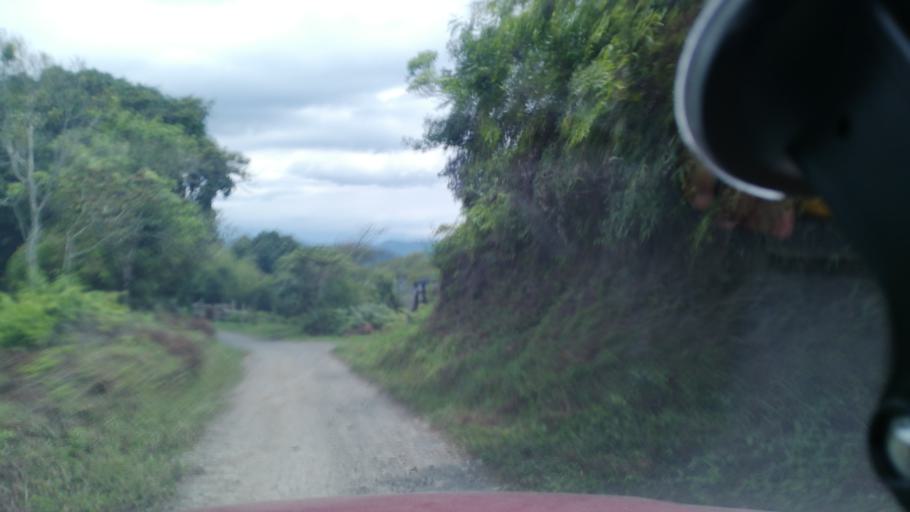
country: CO
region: Cundinamarca
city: Vergara
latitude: 5.1771
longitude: -74.2742
